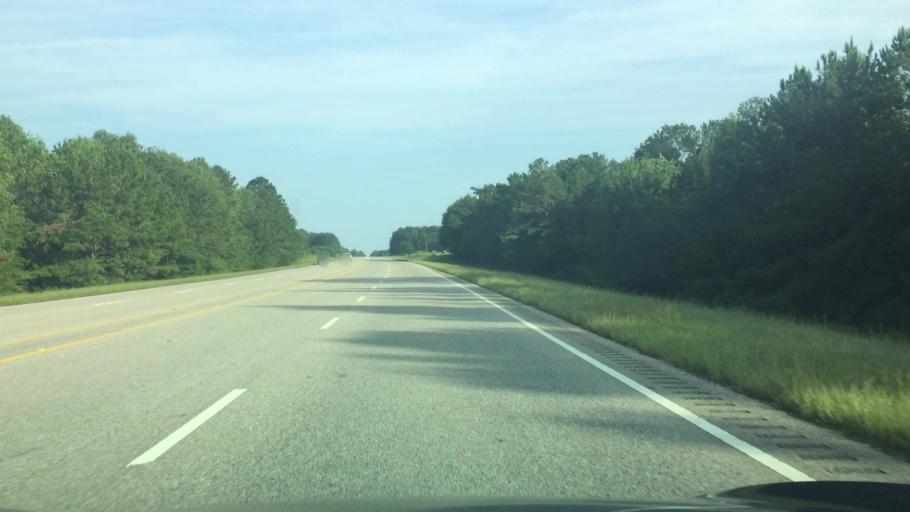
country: US
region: Alabama
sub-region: Butler County
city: Georgiana
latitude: 31.4974
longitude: -86.6916
